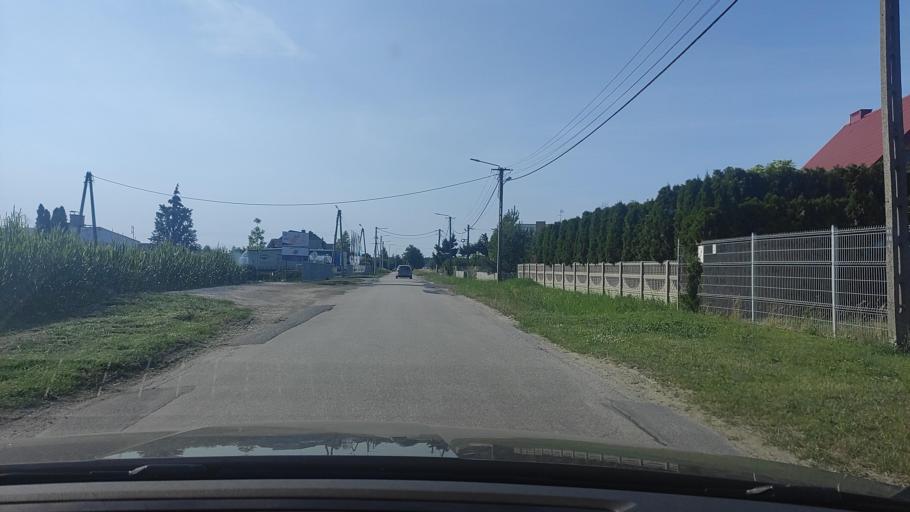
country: PL
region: Greater Poland Voivodeship
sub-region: Powiat poznanski
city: Kostrzyn
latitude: 52.4039
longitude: 17.2224
